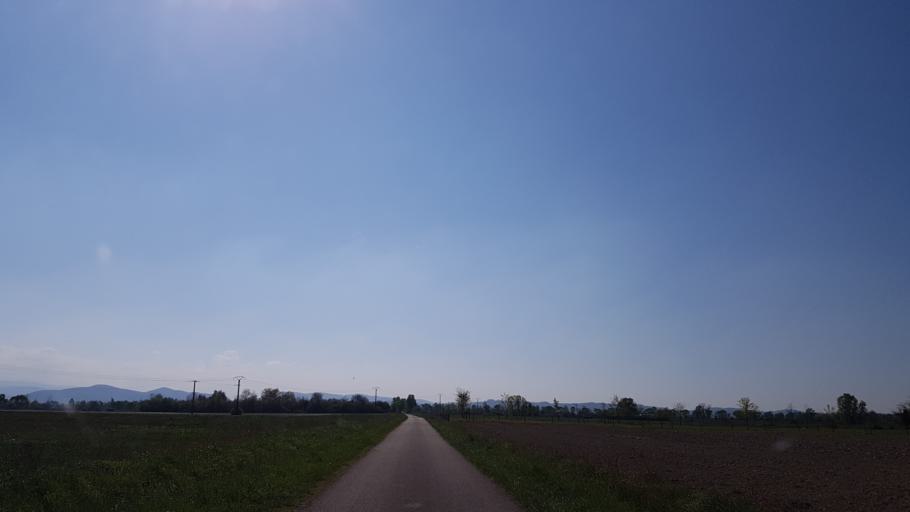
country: FR
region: Midi-Pyrenees
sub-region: Departement de l'Ariege
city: La Tour-du-Crieu
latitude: 43.0868
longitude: 1.6947
